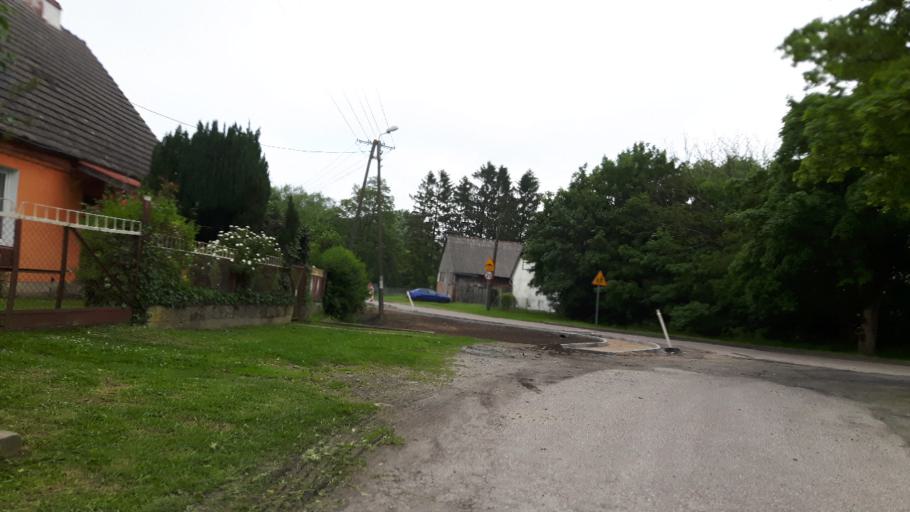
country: PL
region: West Pomeranian Voivodeship
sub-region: Powiat koszalinski
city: Sianow
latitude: 54.2973
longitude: 16.2769
